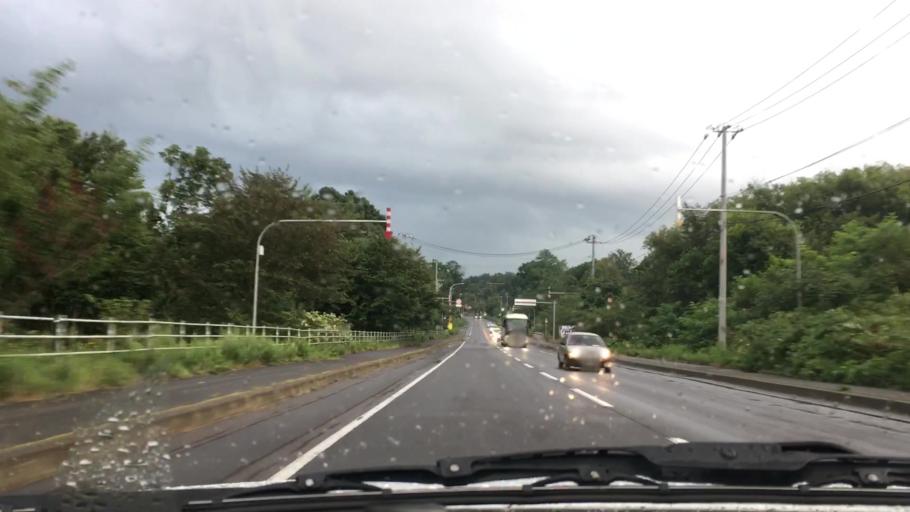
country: JP
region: Hokkaido
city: Nanae
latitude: 42.0861
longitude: 140.5840
